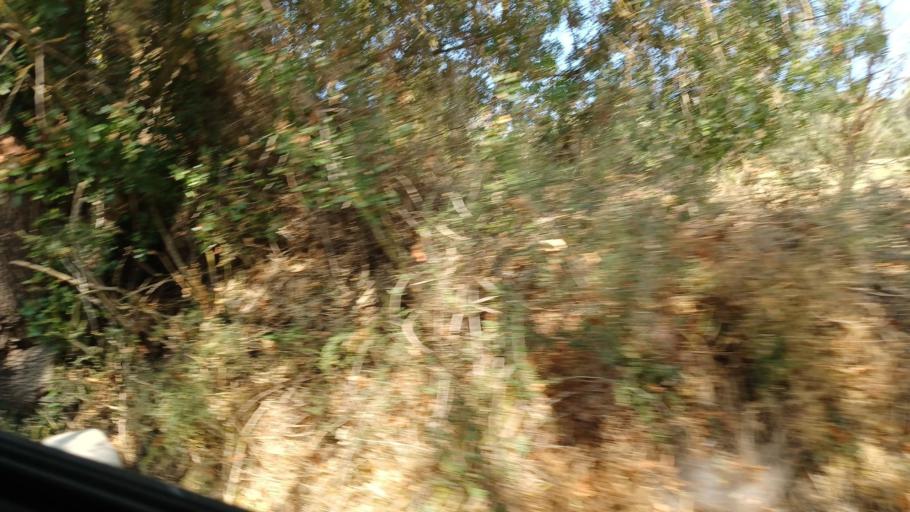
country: CY
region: Pafos
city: Tala
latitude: 34.9181
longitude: 32.4777
